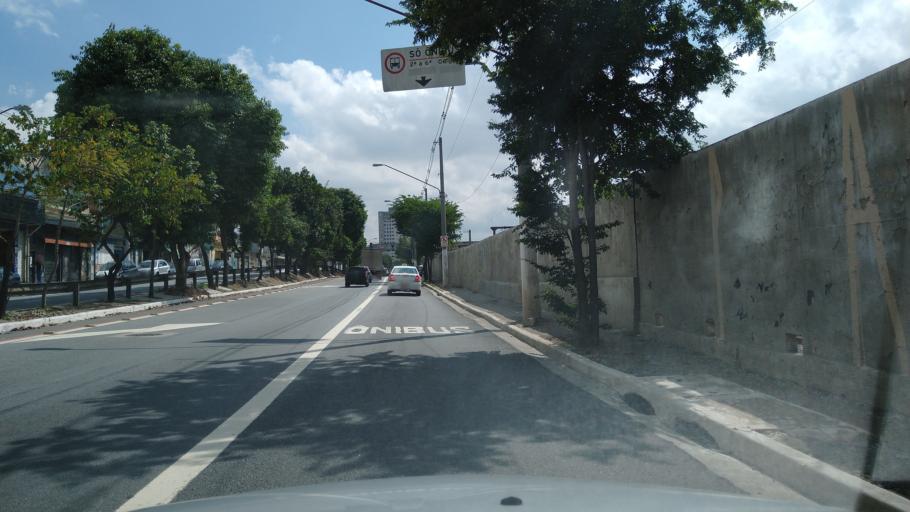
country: BR
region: Sao Paulo
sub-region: Guarulhos
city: Guarulhos
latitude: -23.4854
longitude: -46.4859
